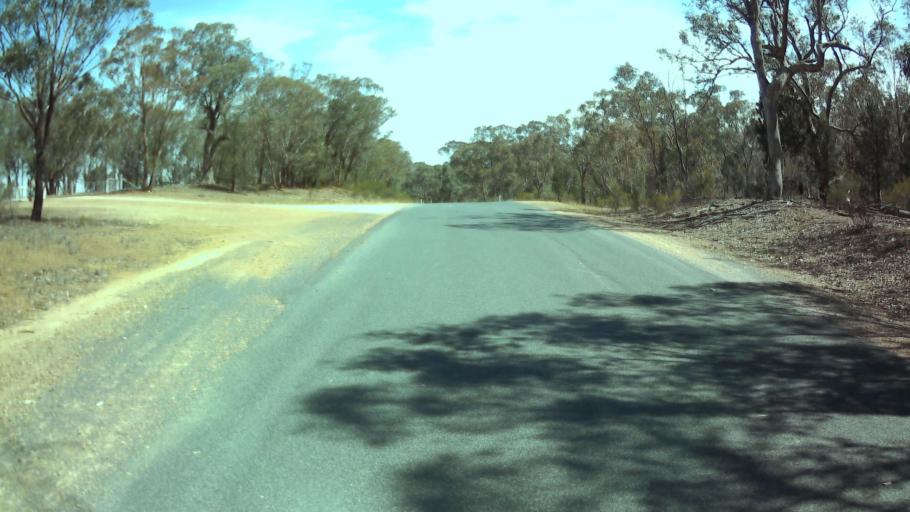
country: AU
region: New South Wales
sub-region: Weddin
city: Grenfell
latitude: -34.0046
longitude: 148.1302
